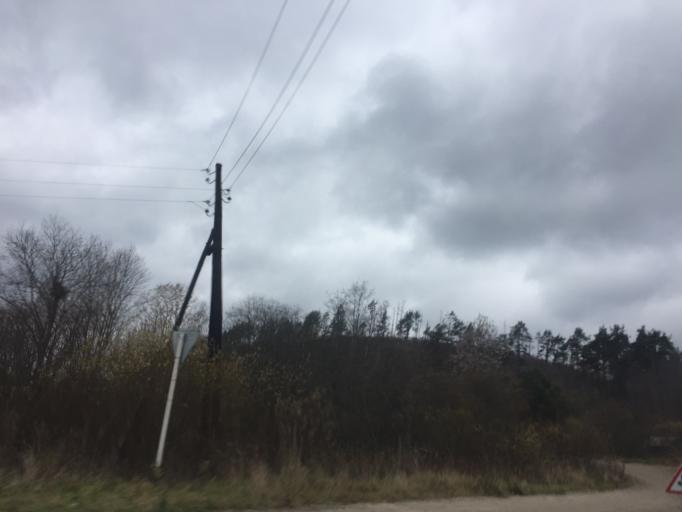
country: RU
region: Republic of Karelia
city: Lakhdenpokh'ya
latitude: 61.4398
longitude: 30.1486
